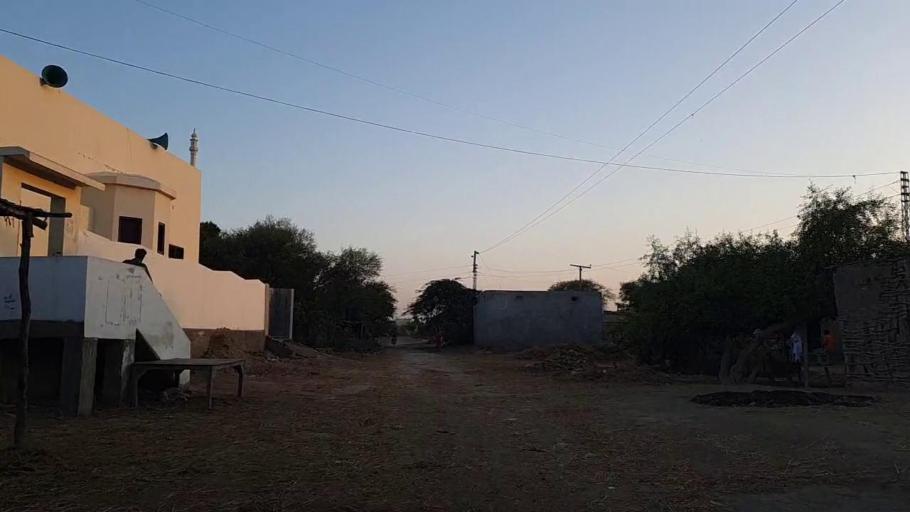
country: PK
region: Sindh
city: Mirpur Batoro
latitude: 24.6447
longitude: 68.1899
